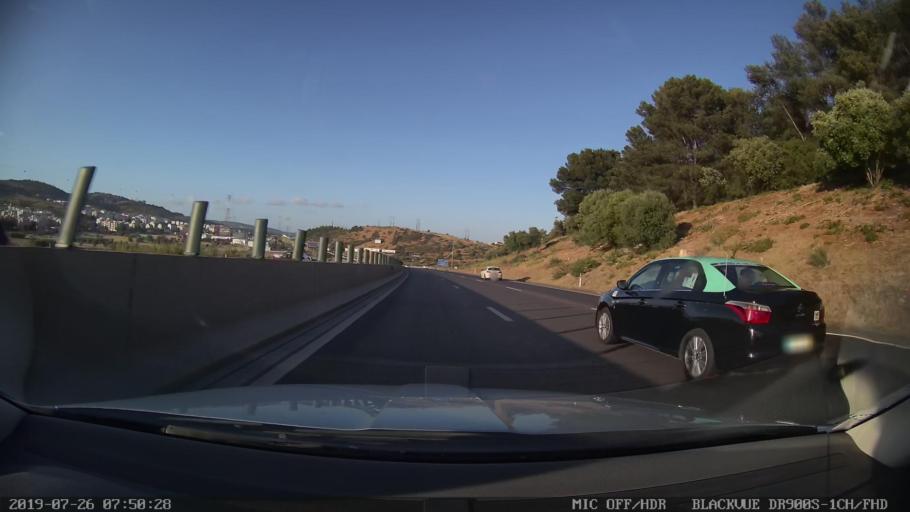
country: PT
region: Lisbon
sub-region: Vila Franca de Xira
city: Vialonga
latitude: 38.8692
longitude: -9.0736
